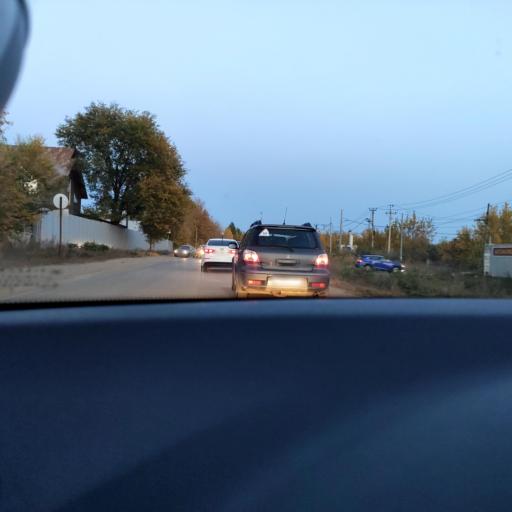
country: RU
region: Samara
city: Novosemeykino
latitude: 53.3688
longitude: 50.3591
